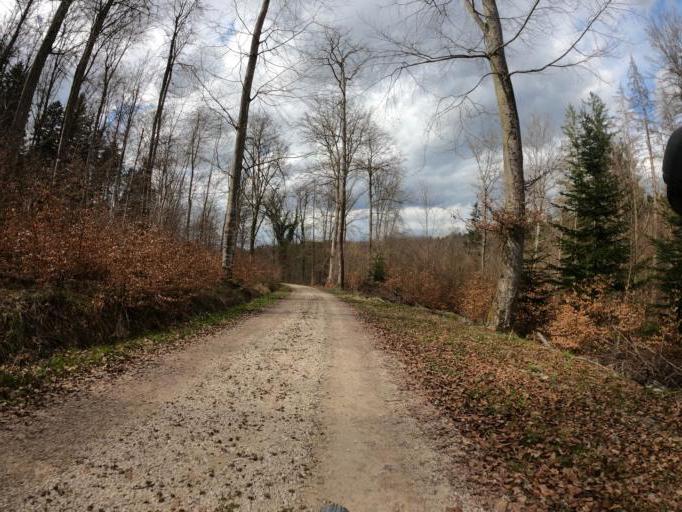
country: DE
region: Baden-Wuerttemberg
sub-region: Tuebingen Region
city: Gomaringen
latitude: 48.4344
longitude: 9.1155
